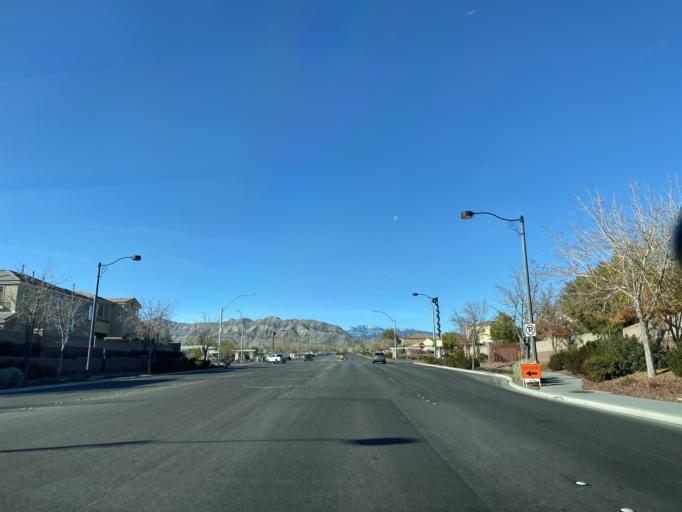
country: US
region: Nevada
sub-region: Clark County
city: Summerlin South
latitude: 36.2994
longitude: -115.3184
